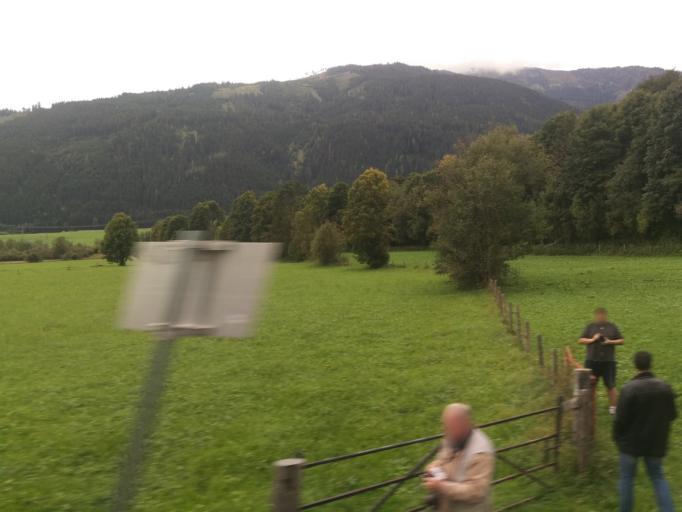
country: AT
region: Salzburg
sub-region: Politischer Bezirk Zell am See
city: Stuhlfelden
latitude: 47.2863
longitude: 12.5367
